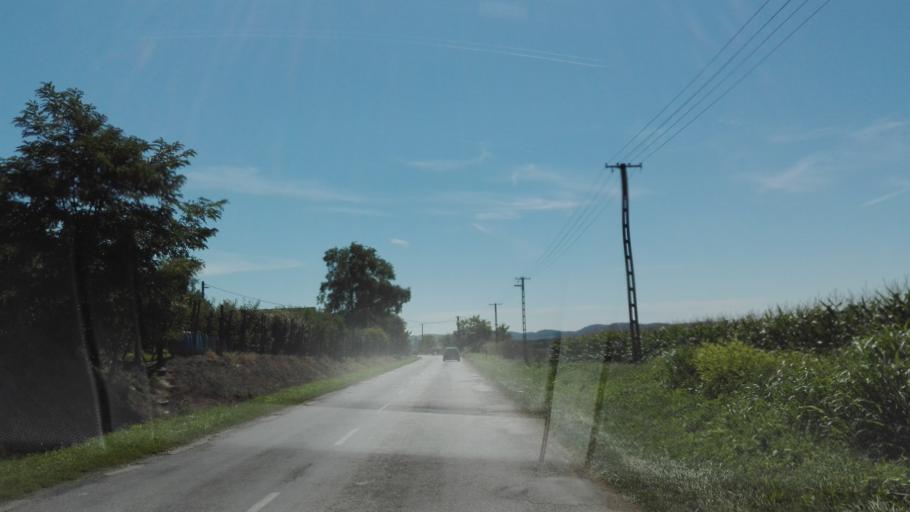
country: HU
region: Tolna
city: Ozora
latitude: 46.7539
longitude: 18.4375
